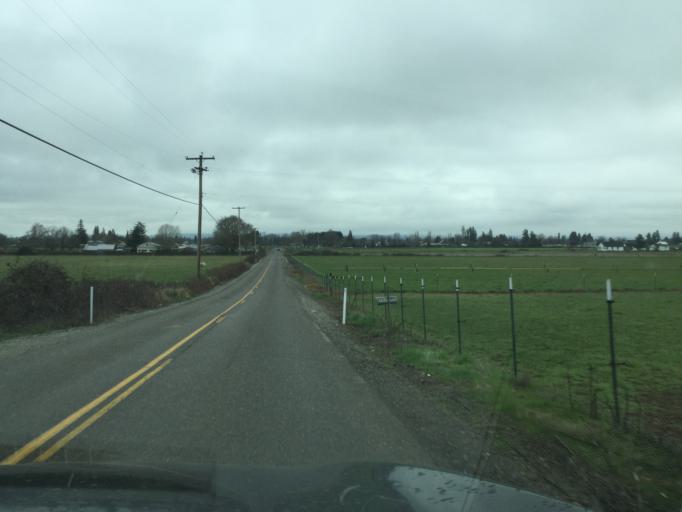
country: US
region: Oregon
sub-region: Jackson County
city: Central Point
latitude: 42.3897
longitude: -122.9499
